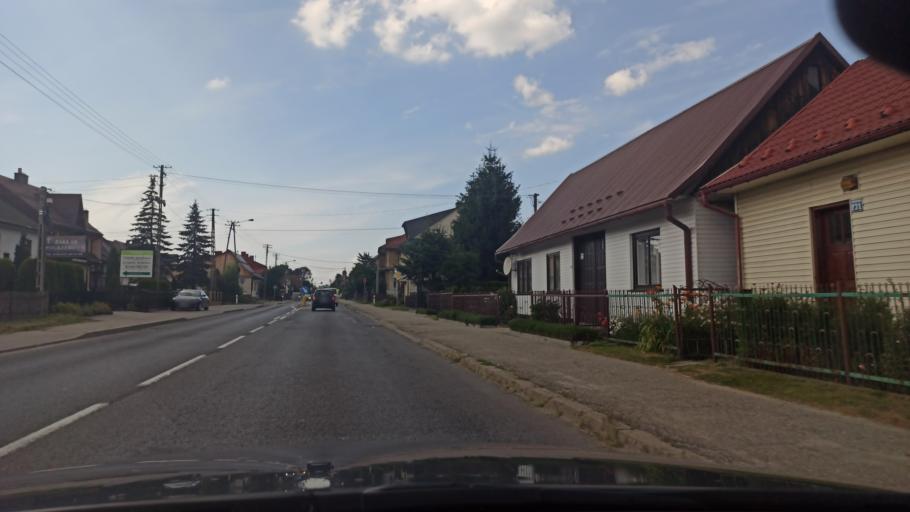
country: PL
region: Lesser Poland Voivodeship
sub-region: Powiat nowotarski
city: Waksmund
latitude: 49.4797
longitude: 20.0829
